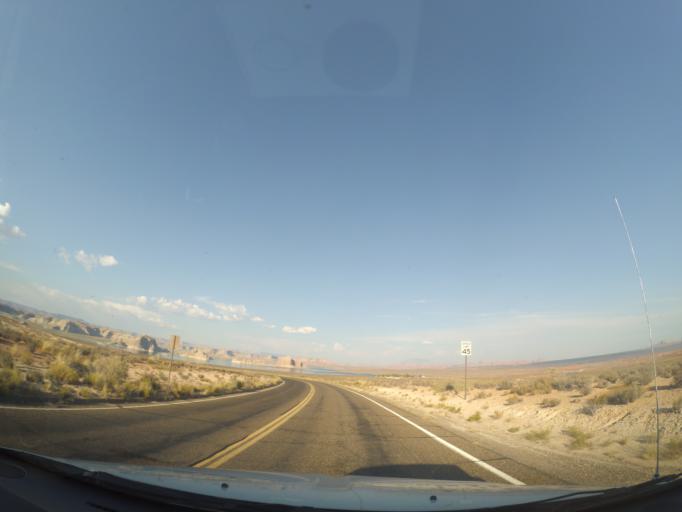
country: US
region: Arizona
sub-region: Coconino County
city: Page
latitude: 36.9893
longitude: -111.5134
